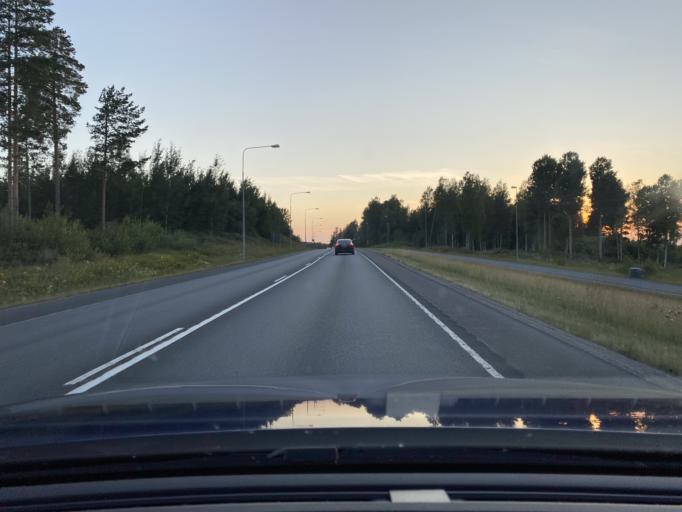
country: FI
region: Pirkanmaa
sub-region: Luoteis-Pirkanmaa
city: Ikaalinen
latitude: 61.7547
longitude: 23.0615
